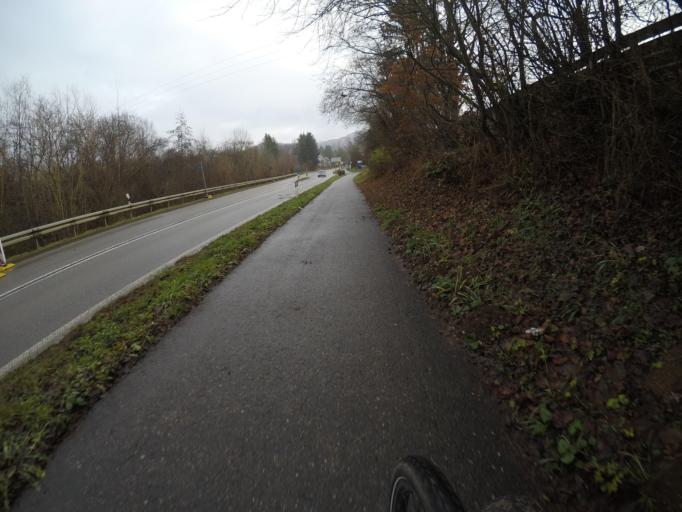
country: DE
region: Baden-Wuerttemberg
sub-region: Regierungsbezirk Stuttgart
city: Beuren
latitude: 48.5751
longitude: 9.3922
